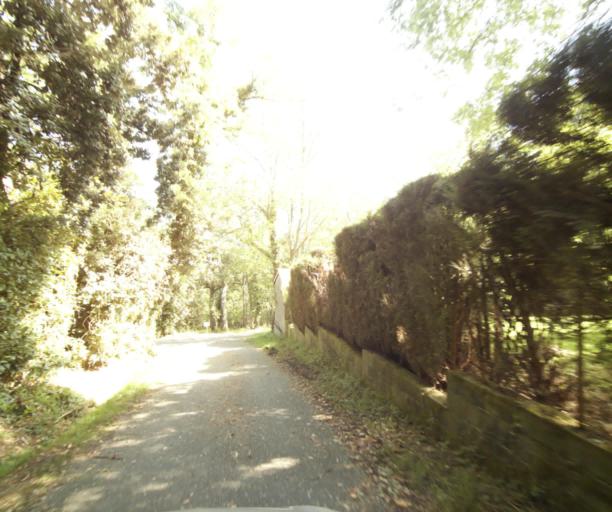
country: FR
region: Aquitaine
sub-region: Departement des Pyrenees-Atlantiques
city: Villefranque
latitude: 43.4567
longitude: -1.4429
